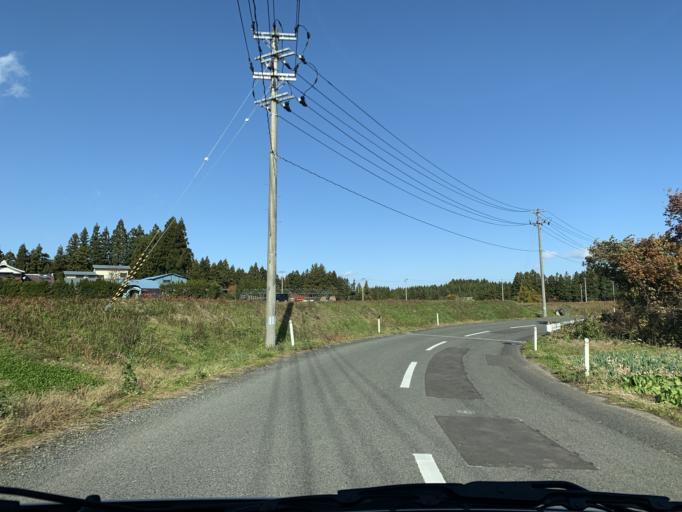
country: JP
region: Iwate
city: Mizusawa
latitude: 39.0683
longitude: 141.1116
